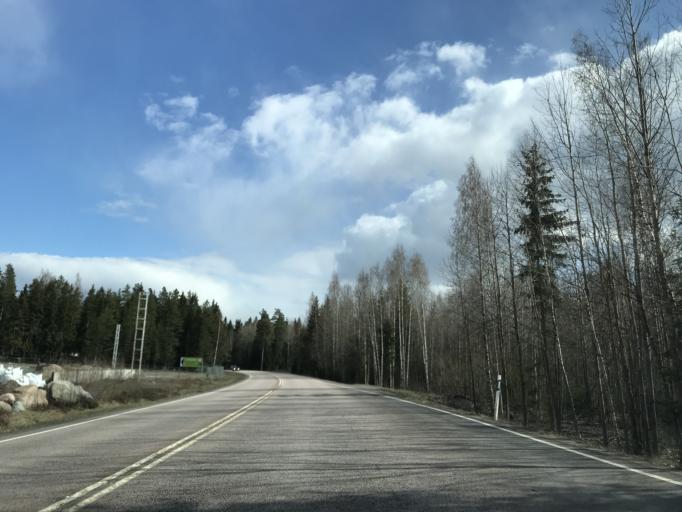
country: FI
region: Uusimaa
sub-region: Helsinki
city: Hyvinge
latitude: 60.5444
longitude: 24.8622
